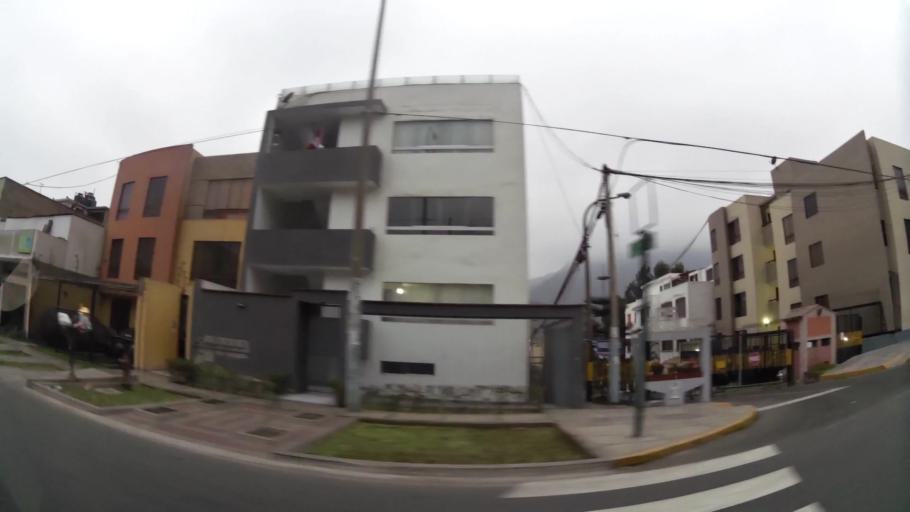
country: PE
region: Lima
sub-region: Lima
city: La Molina
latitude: -12.1111
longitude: -76.9424
